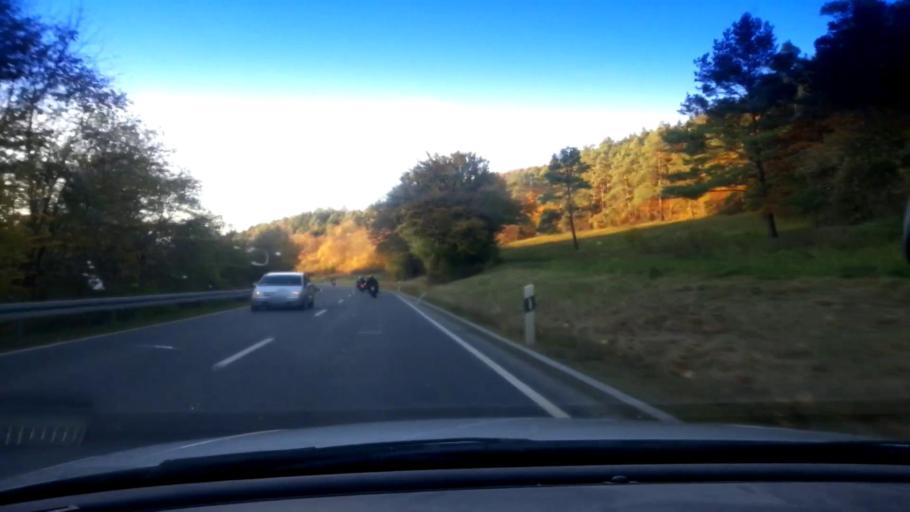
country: DE
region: Bavaria
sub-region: Upper Franconia
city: Heiligenstadt
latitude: 49.8474
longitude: 11.1895
